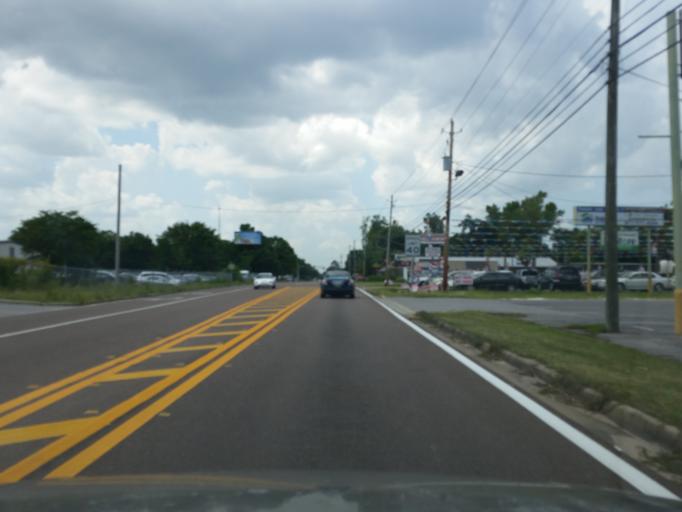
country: US
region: Florida
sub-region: Escambia County
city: Brent
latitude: 30.4728
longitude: -87.2445
